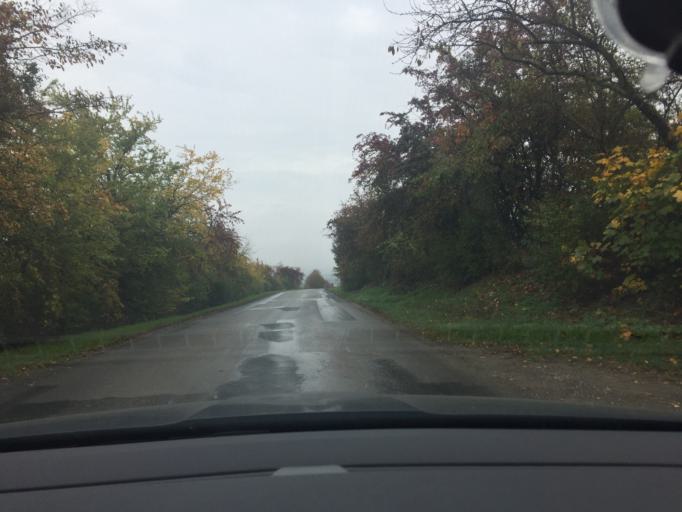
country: CZ
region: South Moravian
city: Sokolnice
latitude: 49.1290
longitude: 16.7609
